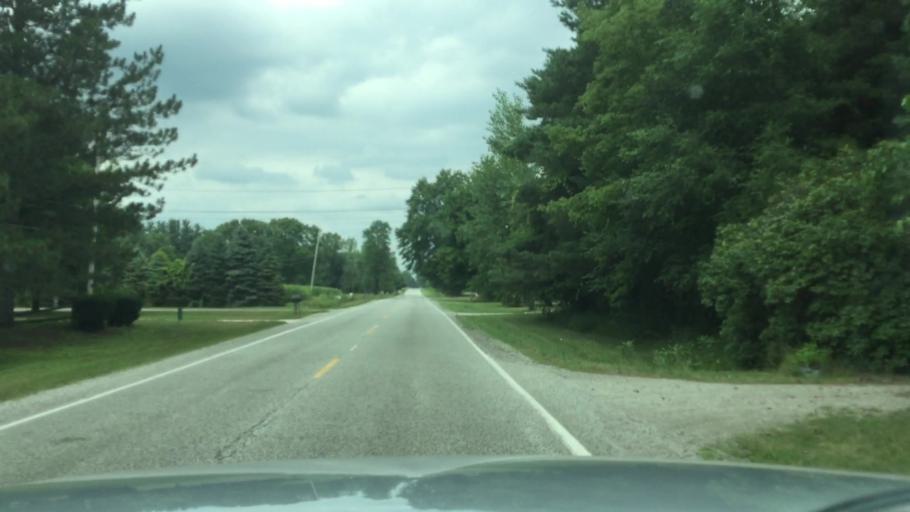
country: US
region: Michigan
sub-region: Saginaw County
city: Bridgeport
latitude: 43.3114
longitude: -83.8945
